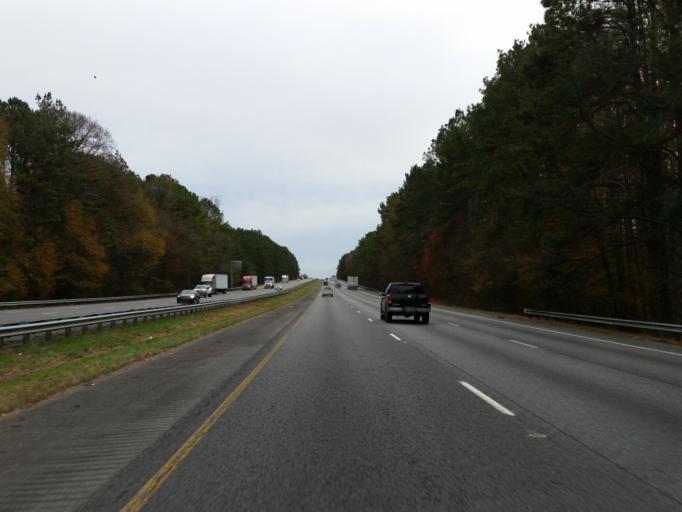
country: US
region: Georgia
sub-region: Monroe County
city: Forsyth
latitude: 33.1045
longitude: -84.0012
